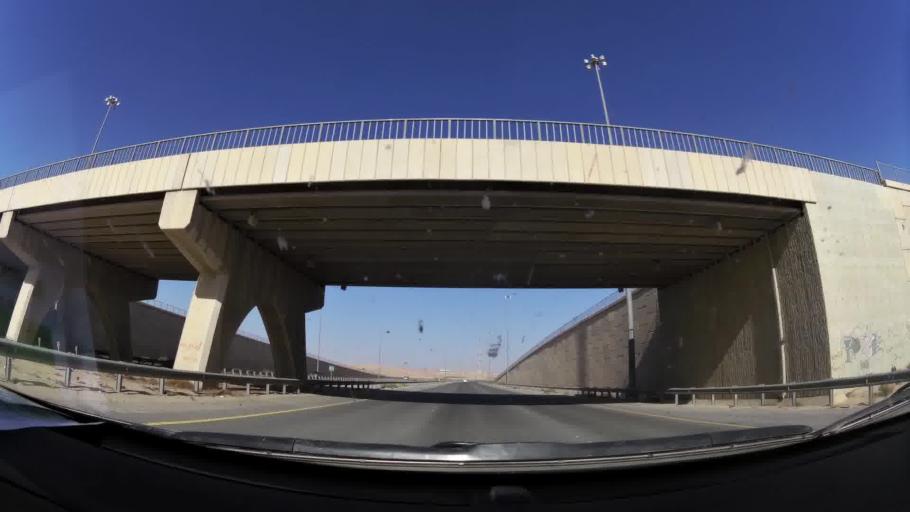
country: KW
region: Muhafazat al Jahra'
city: Al Jahra'
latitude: 29.4748
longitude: 47.7686
